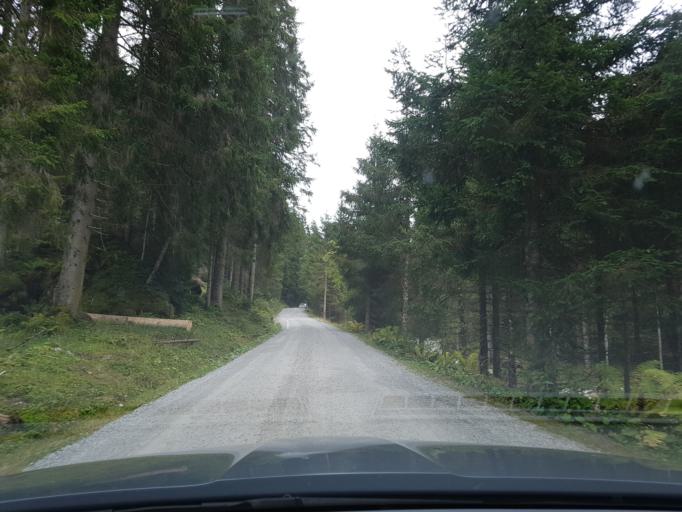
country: AT
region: Salzburg
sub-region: Politischer Bezirk Sankt Johann im Pongau
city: Forstau
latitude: 47.3350
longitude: 13.5774
